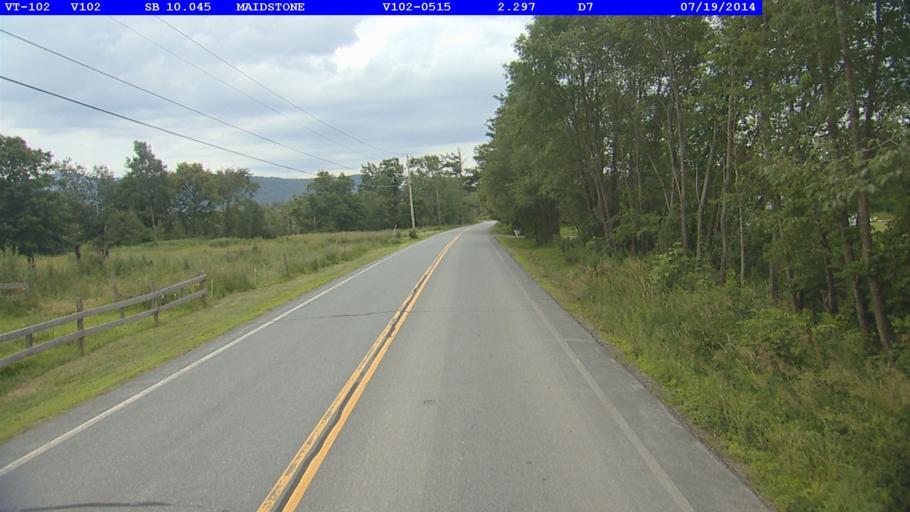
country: US
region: Vermont
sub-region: Essex County
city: Guildhall
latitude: 44.5969
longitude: -71.5605
